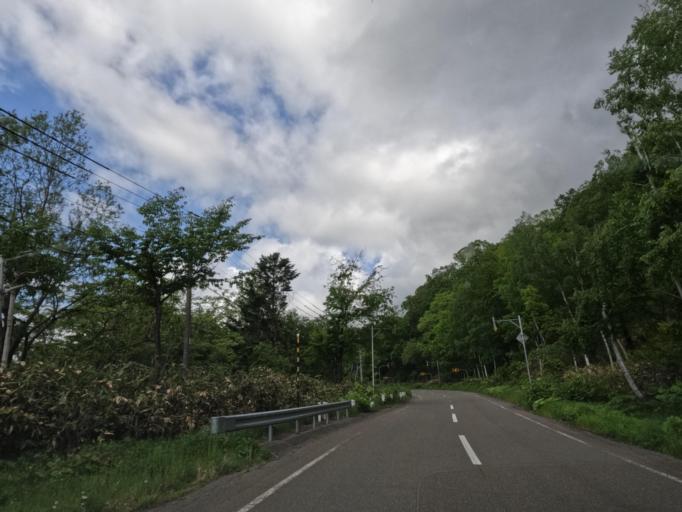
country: JP
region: Hokkaido
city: Tobetsu
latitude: 43.4849
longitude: 141.6048
